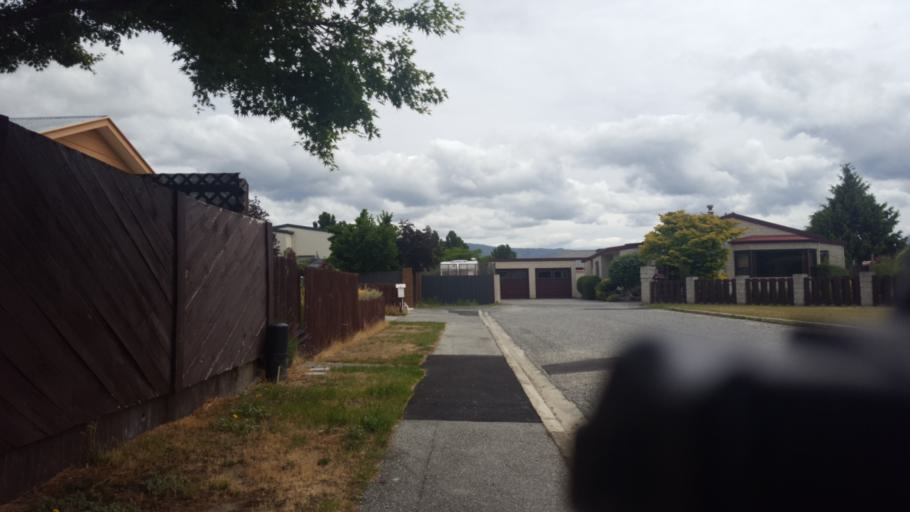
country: NZ
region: Otago
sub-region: Queenstown-Lakes District
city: Wanaka
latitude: -45.2547
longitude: 169.3863
